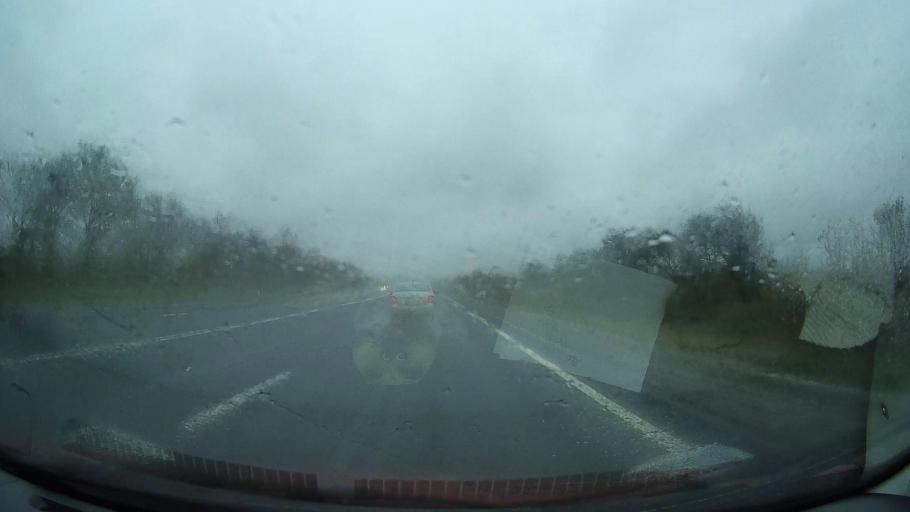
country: RU
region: Stavropol'skiy
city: Nevinnomyssk
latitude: 44.6195
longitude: 42.0935
